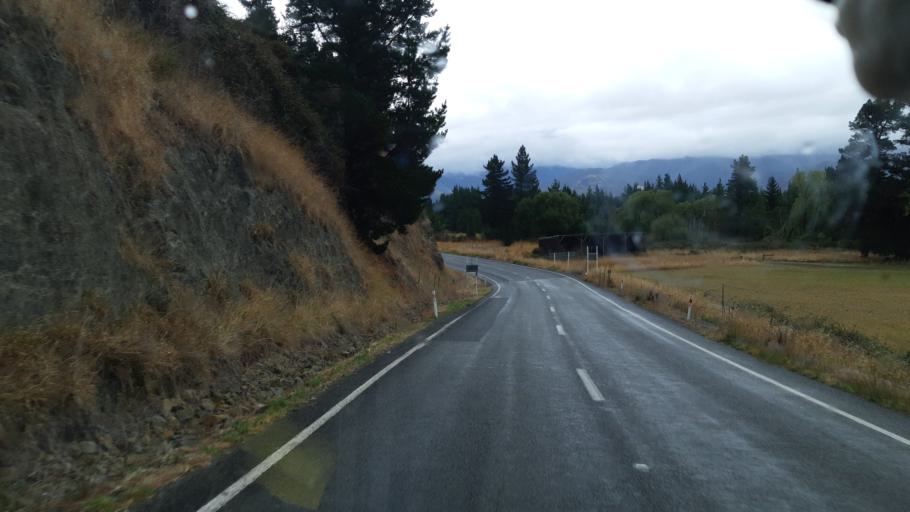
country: NZ
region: Canterbury
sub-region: Hurunui District
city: Amberley
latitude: -42.5816
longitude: 172.7735
